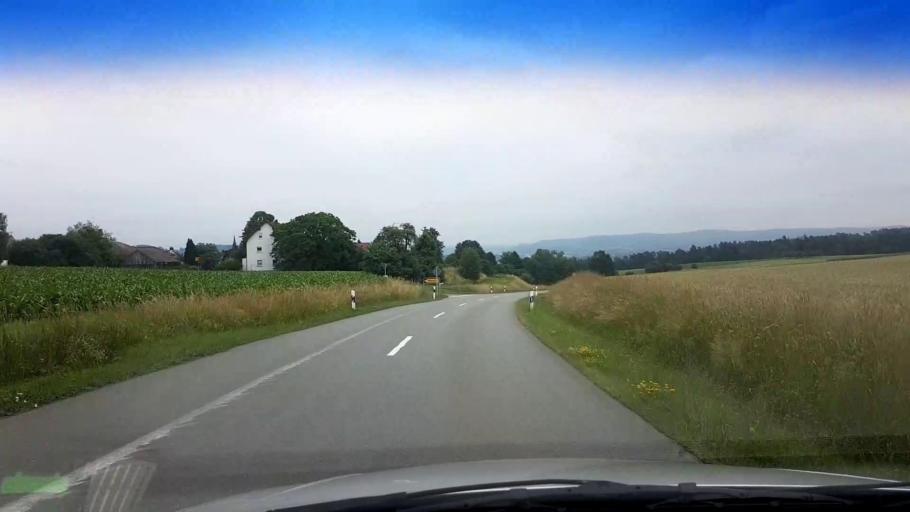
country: DE
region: Bavaria
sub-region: Upper Franconia
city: Mainleus
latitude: 50.0938
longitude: 11.3514
